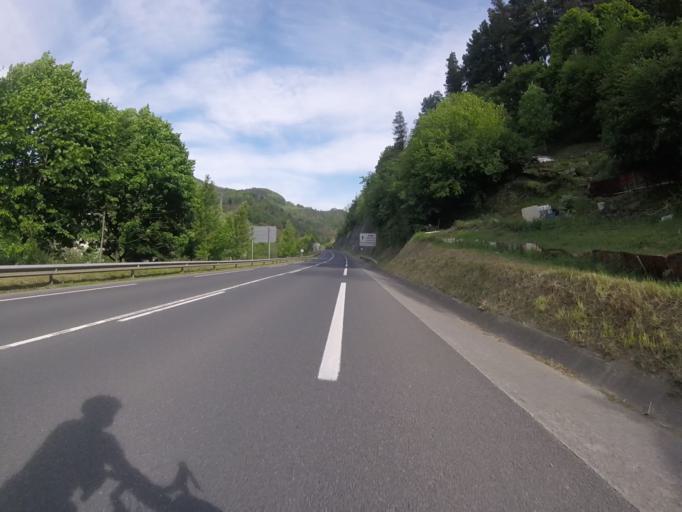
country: ES
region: Basque Country
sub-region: Provincia de Guipuzcoa
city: Urretxu
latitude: 43.0962
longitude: -2.3139
